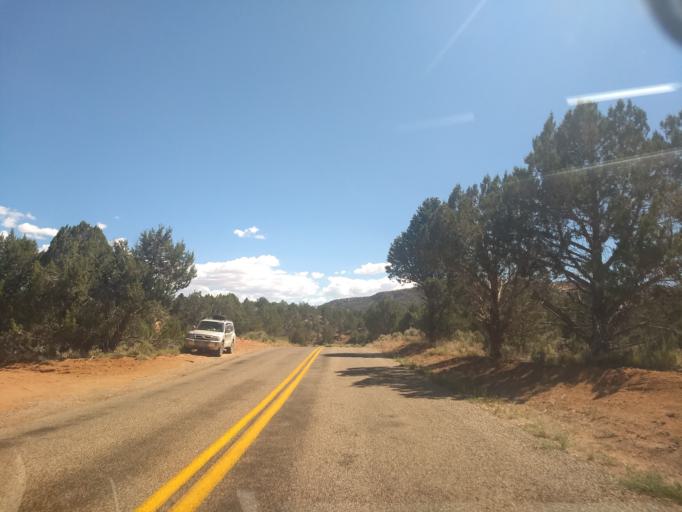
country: US
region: Utah
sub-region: Washington County
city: Hildale
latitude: 36.9917
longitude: -112.8661
